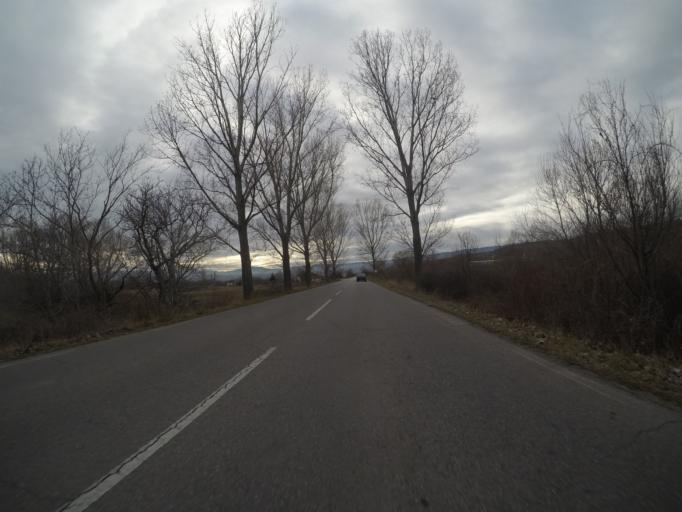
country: BG
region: Kyustendil
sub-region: Obshtina Kocherinovo
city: Kocherinovo
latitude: 42.0954
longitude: 23.0763
